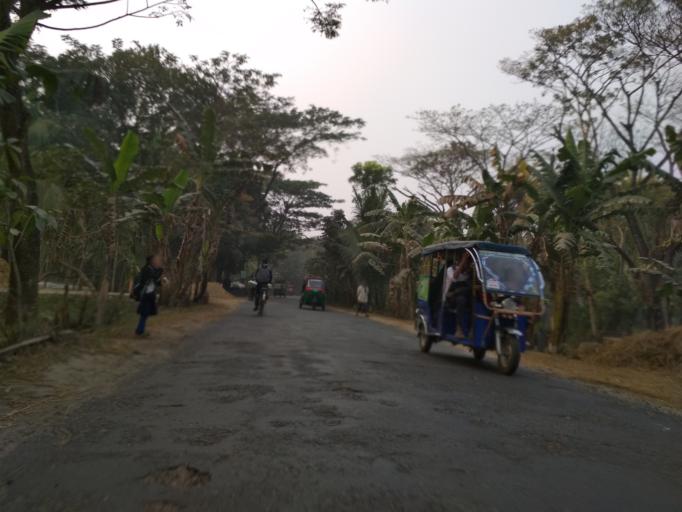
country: BD
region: Chittagong
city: Lakshmipur
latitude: 22.9228
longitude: 90.8355
